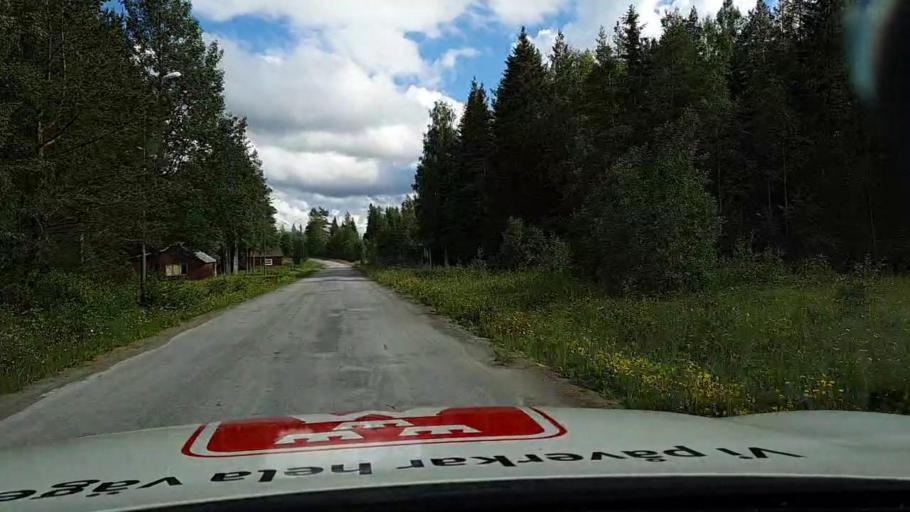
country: SE
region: Jaemtland
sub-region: OEstersunds Kommun
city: Brunflo
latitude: 63.1300
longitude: 15.0777
